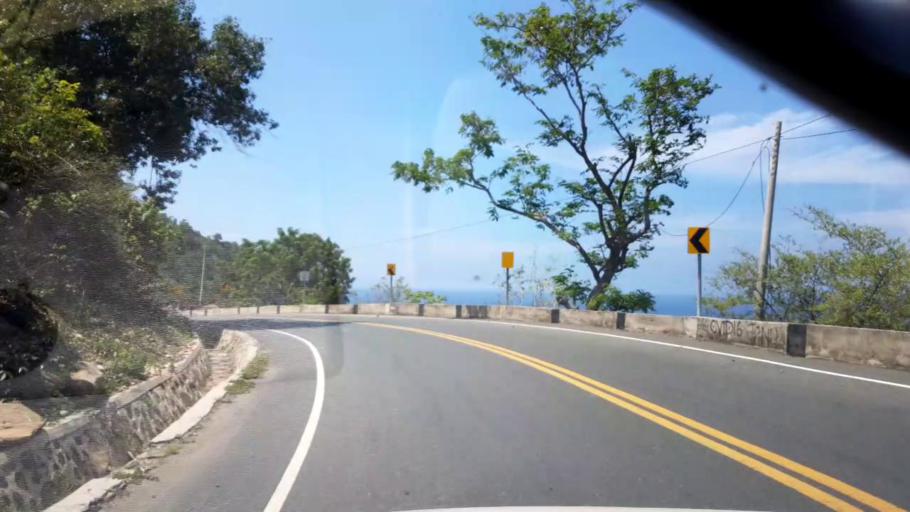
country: TL
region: Liquica
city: Maubara
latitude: -8.6590
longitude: 125.1151
